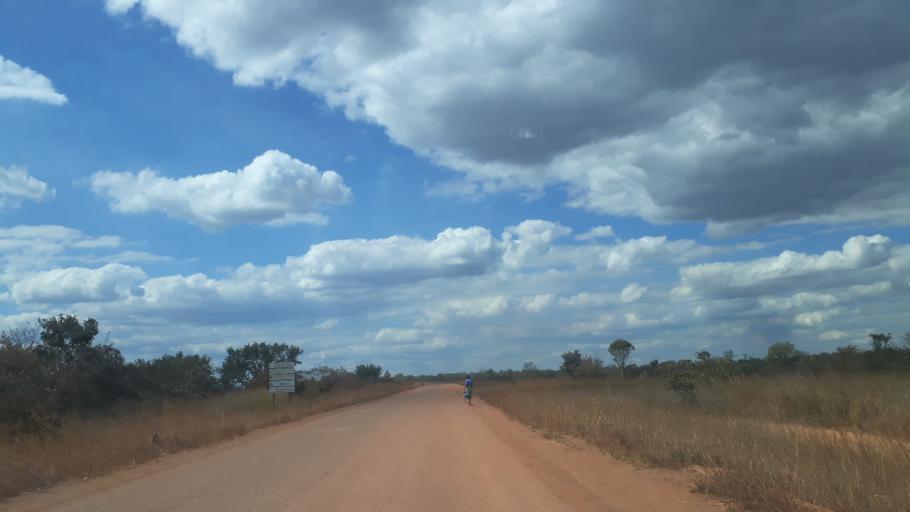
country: ZM
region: Copperbelt
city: Mufulira
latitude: -11.9963
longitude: 28.7247
